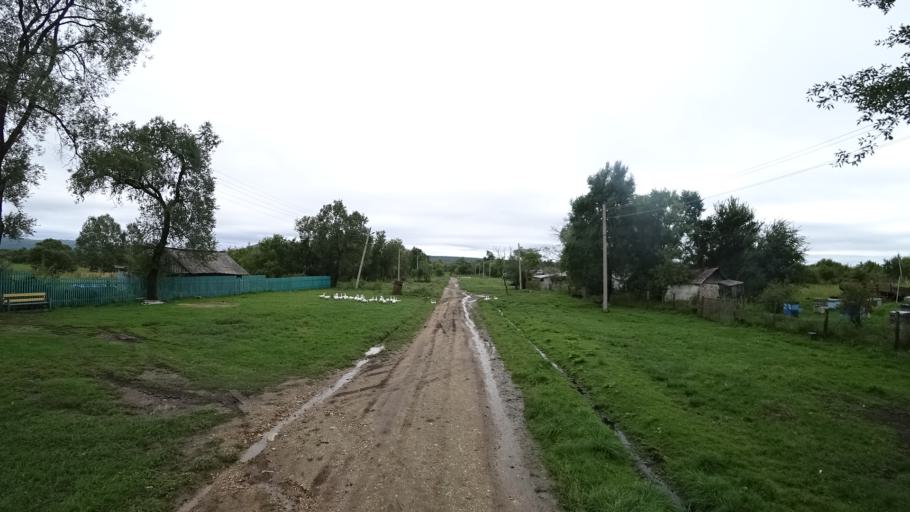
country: RU
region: Primorskiy
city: Rettikhovka
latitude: 44.1368
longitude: 132.6526
